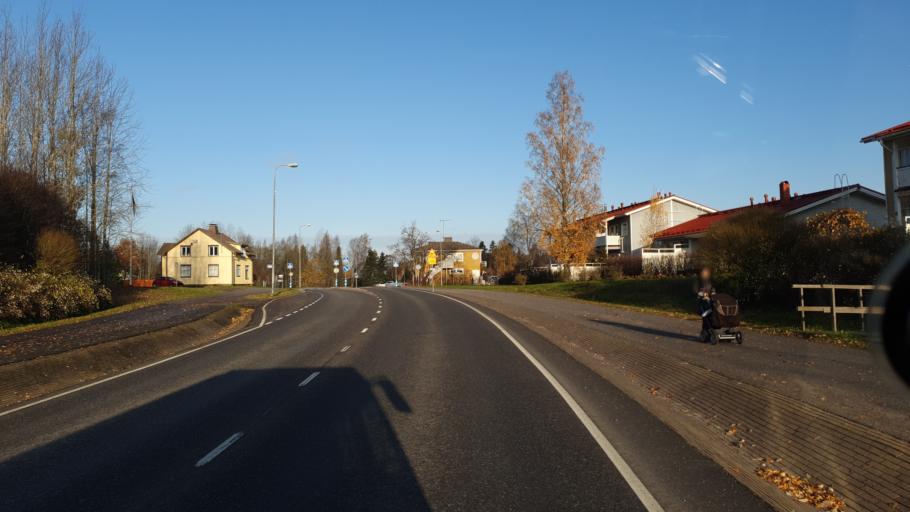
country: FI
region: Uusimaa
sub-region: Helsinki
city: Siuntio
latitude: 60.1416
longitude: 24.2249
